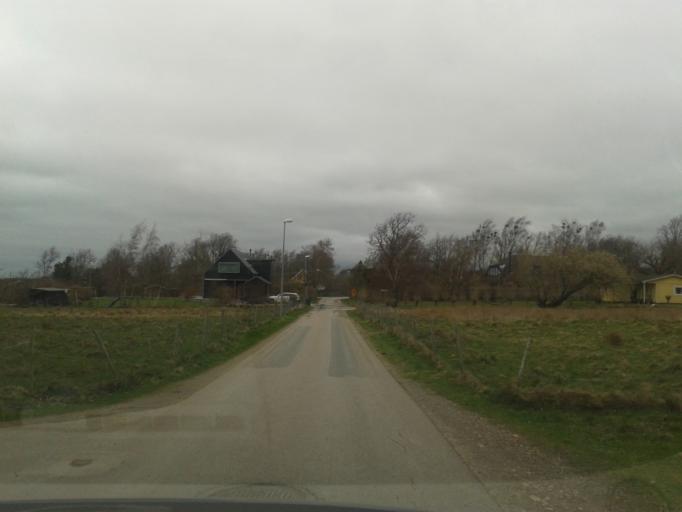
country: SE
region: Skane
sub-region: Angelholms Kommun
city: Vejbystrand
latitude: 56.3262
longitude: 12.7612
